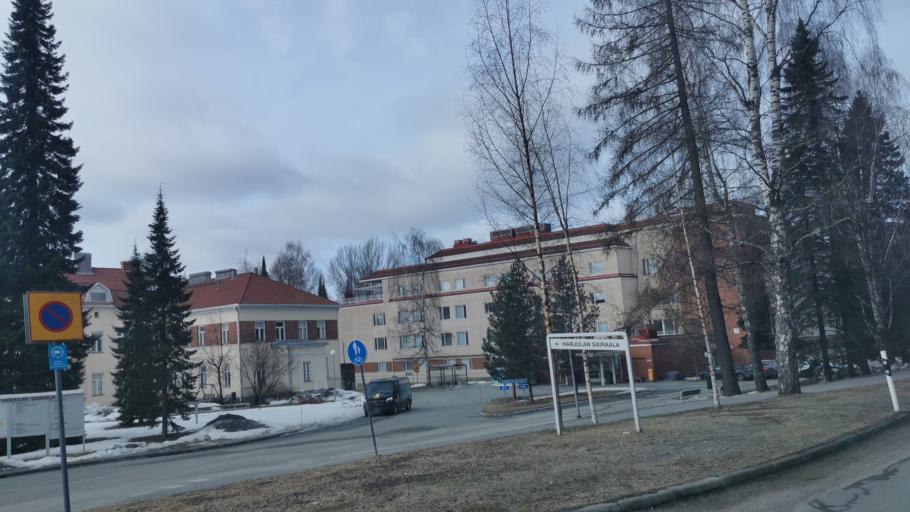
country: FI
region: Northern Savo
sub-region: Kuopio
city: Kuopio
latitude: 62.8976
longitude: 27.6390
